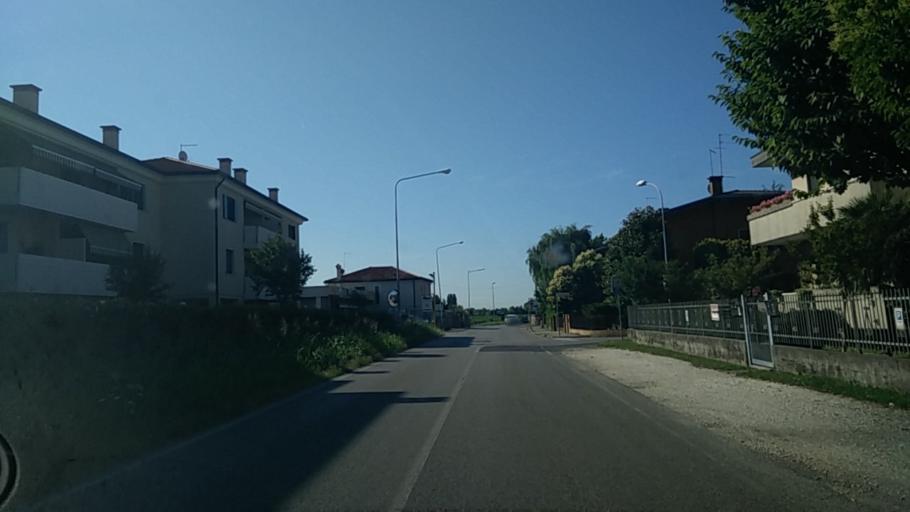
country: IT
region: Veneto
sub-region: Provincia di Venezia
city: Dolo
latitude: 45.4171
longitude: 12.0814
